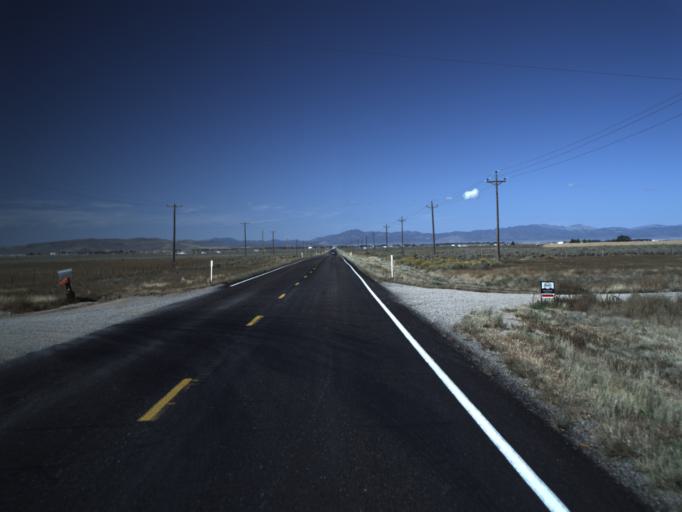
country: US
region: Utah
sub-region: Washington County
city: Enterprise
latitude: 37.6847
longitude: -113.5874
